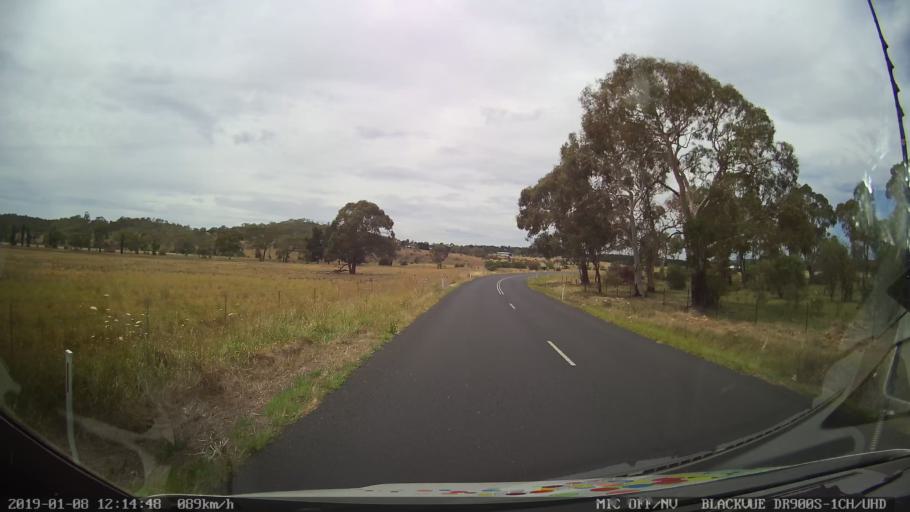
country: AU
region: New South Wales
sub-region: Armidale Dumaresq
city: Armidale
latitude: -30.4800
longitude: 151.6272
